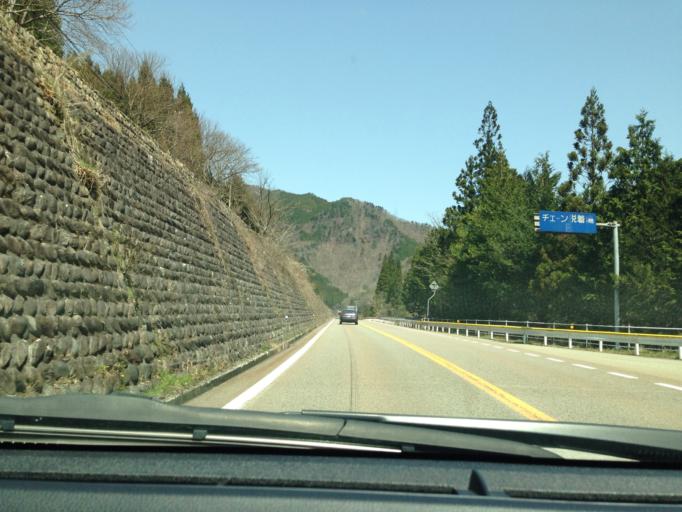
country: JP
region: Gifu
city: Takayama
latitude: 36.0120
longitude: 137.2924
